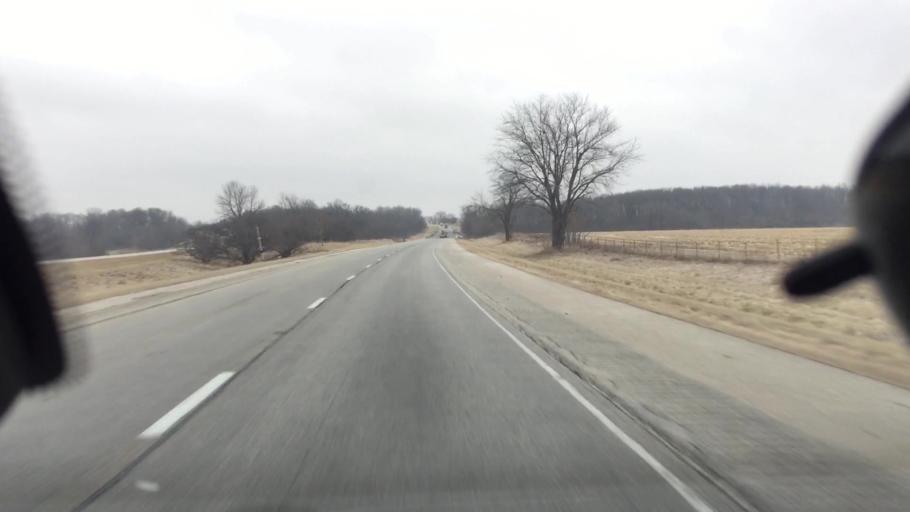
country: US
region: Illinois
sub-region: Knox County
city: Galesburg
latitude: 41.1427
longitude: -90.3326
